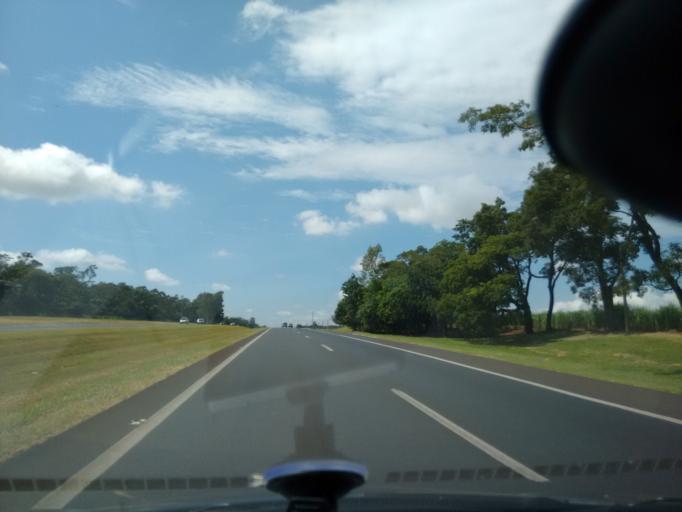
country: BR
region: Sao Paulo
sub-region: Ibate
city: Ibate
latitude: -21.9700
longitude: -47.9532
